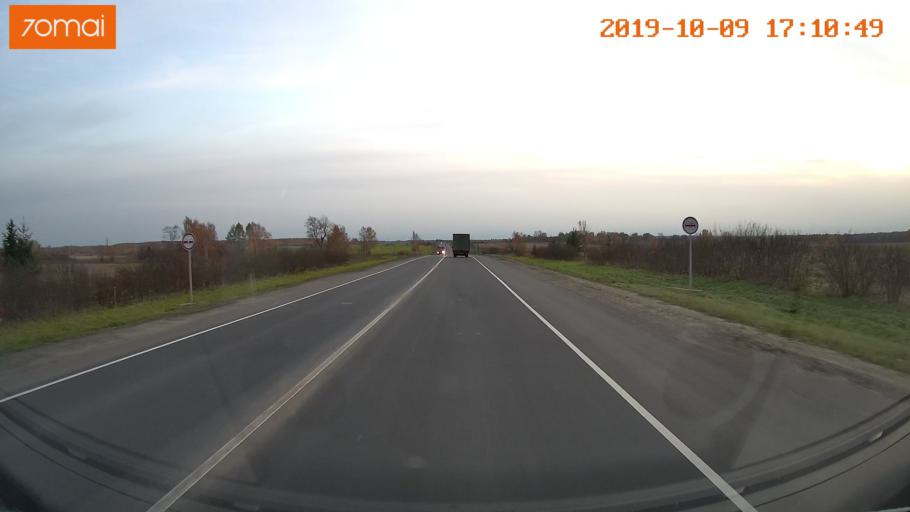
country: RU
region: Ivanovo
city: Privolzhsk
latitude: 57.3508
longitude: 41.2546
